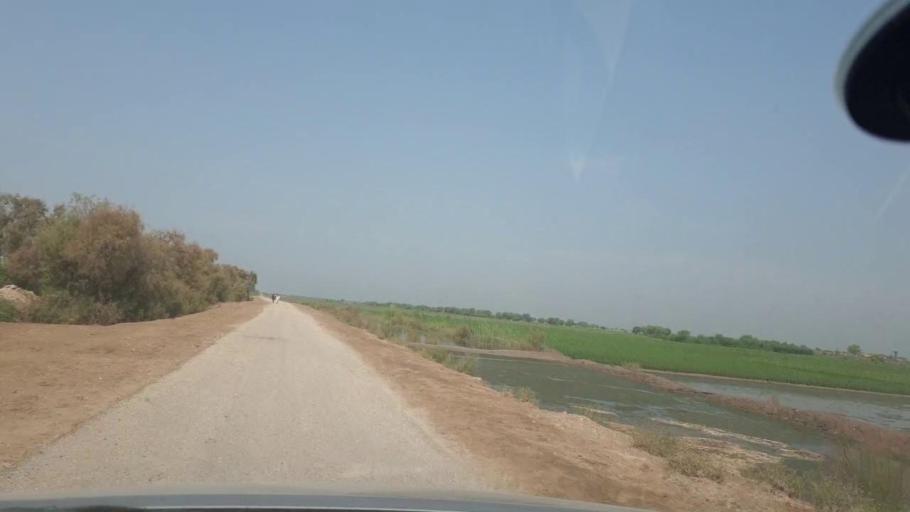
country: PK
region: Balochistan
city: Mehrabpur
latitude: 28.0633
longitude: 68.0650
